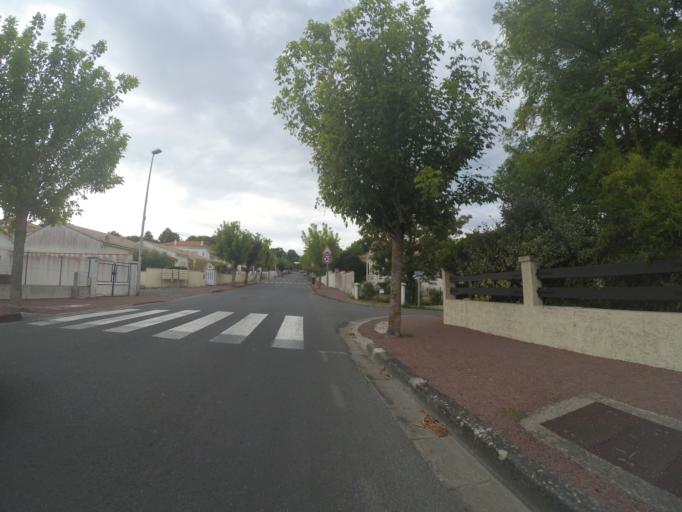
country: FR
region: Poitou-Charentes
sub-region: Departement de la Charente-Maritime
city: Meschers-sur-Gironde
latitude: 45.5637
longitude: -0.9600
